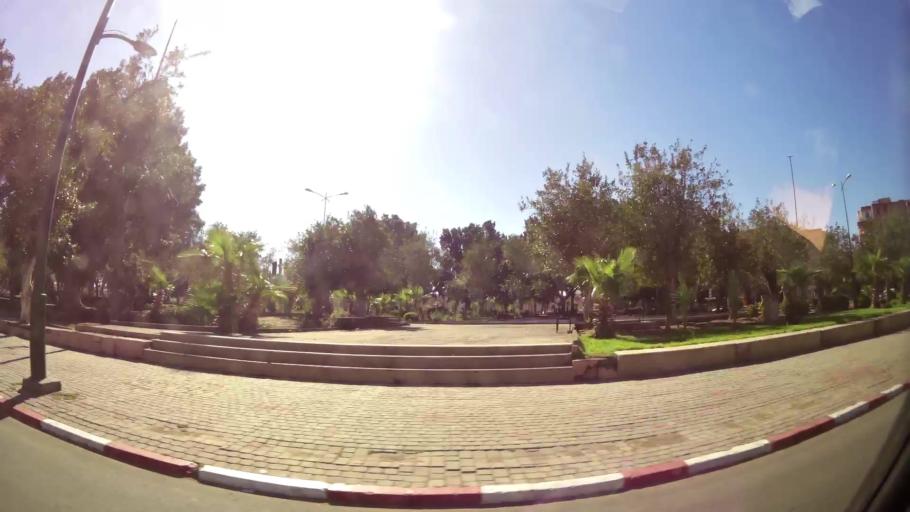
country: MA
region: Marrakech-Tensift-Al Haouz
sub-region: Marrakech
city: Marrakesh
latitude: 31.6346
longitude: -8.0012
